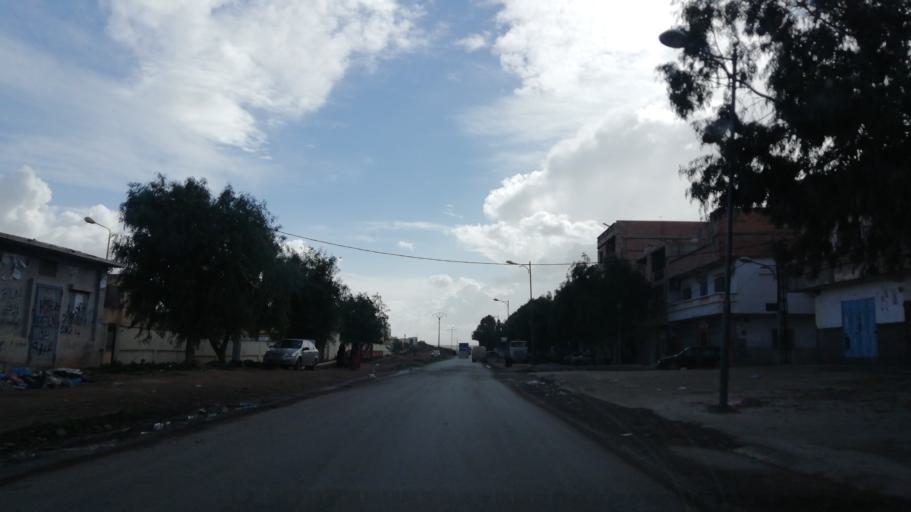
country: DZ
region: Oran
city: Sidi ech Chahmi
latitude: 35.6492
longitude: -0.5635
